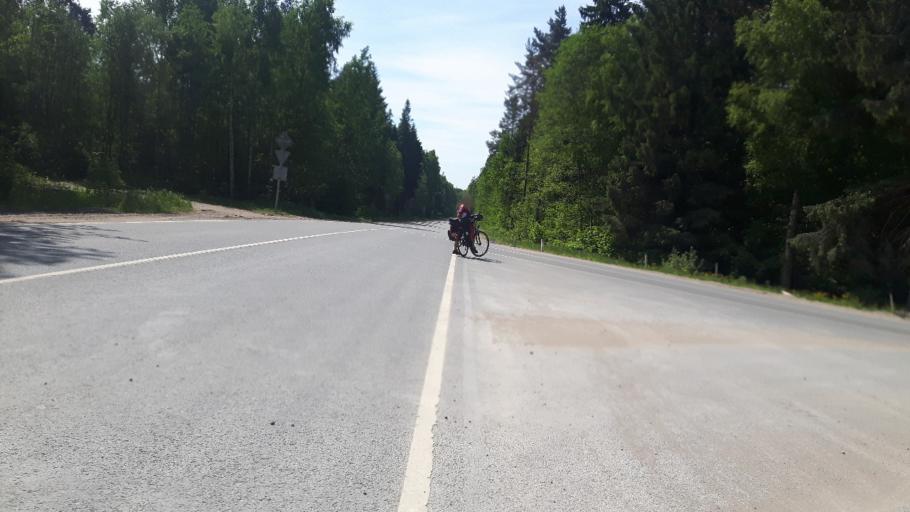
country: RU
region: Leningrad
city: Vistino
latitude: 59.6923
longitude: 28.4621
